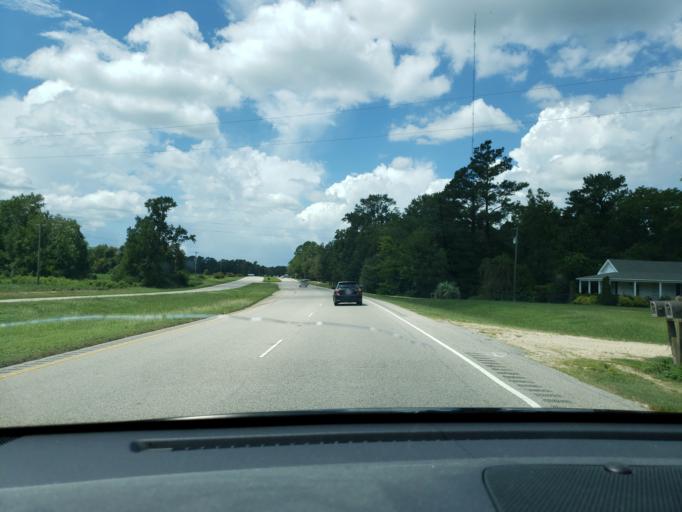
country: US
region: North Carolina
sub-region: Bladen County
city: Bladenboro
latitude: 34.7294
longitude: -78.7783
